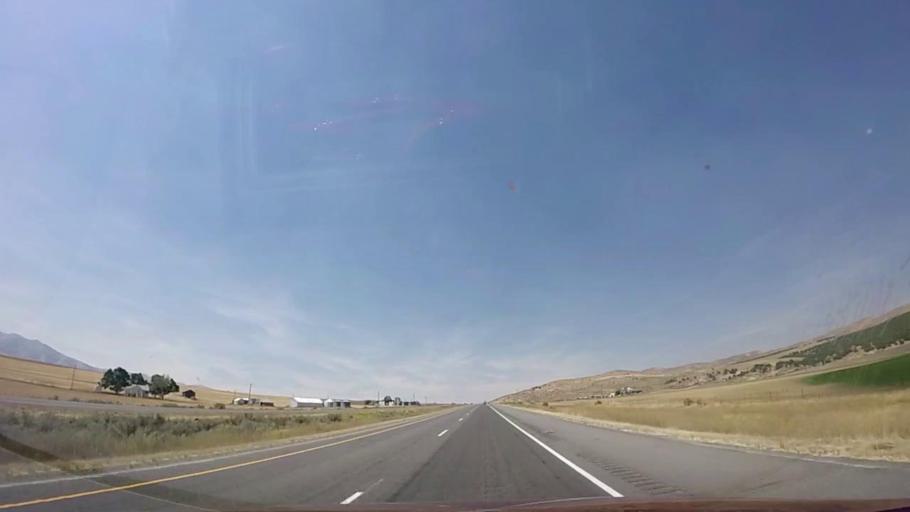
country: US
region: Idaho
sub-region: Power County
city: American Falls
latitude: 42.1669
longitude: -112.9981
